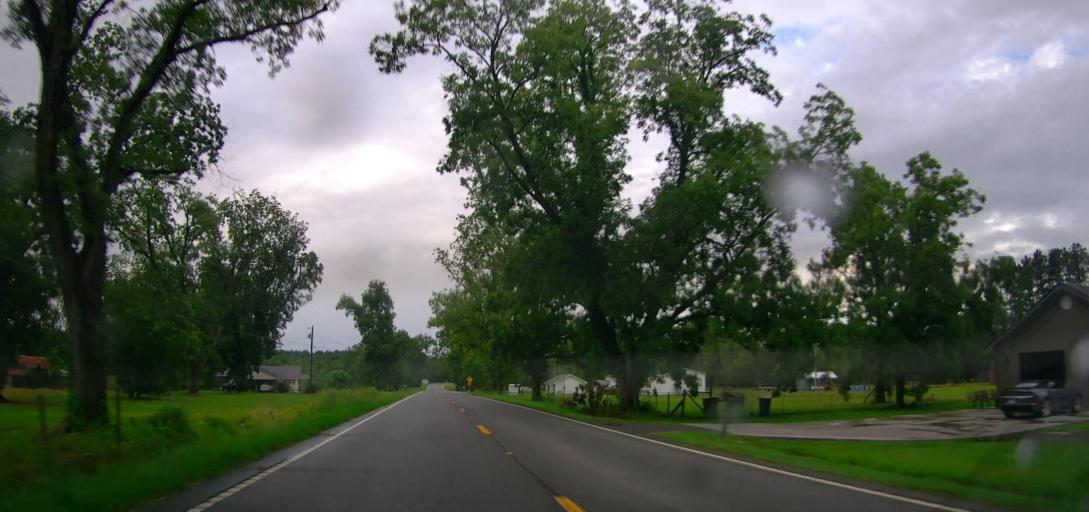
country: US
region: Georgia
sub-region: Ware County
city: Deenwood
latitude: 31.2706
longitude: -82.4062
